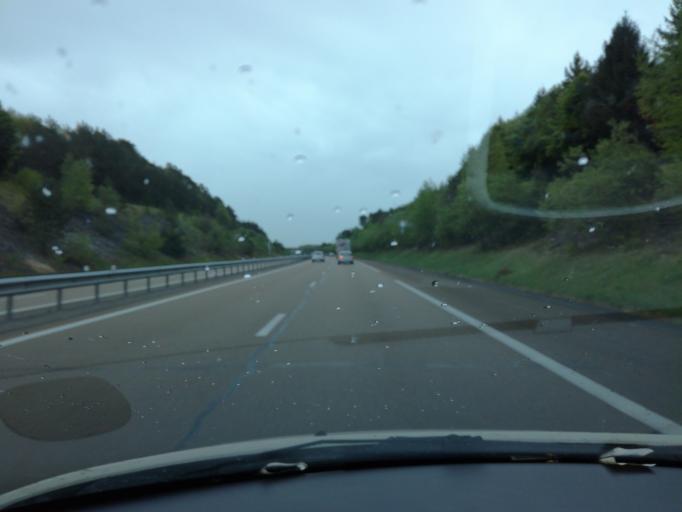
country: FR
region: Champagne-Ardenne
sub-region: Departement de la Haute-Marne
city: Chamarandes-Choignes
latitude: 48.0114
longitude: 5.1023
